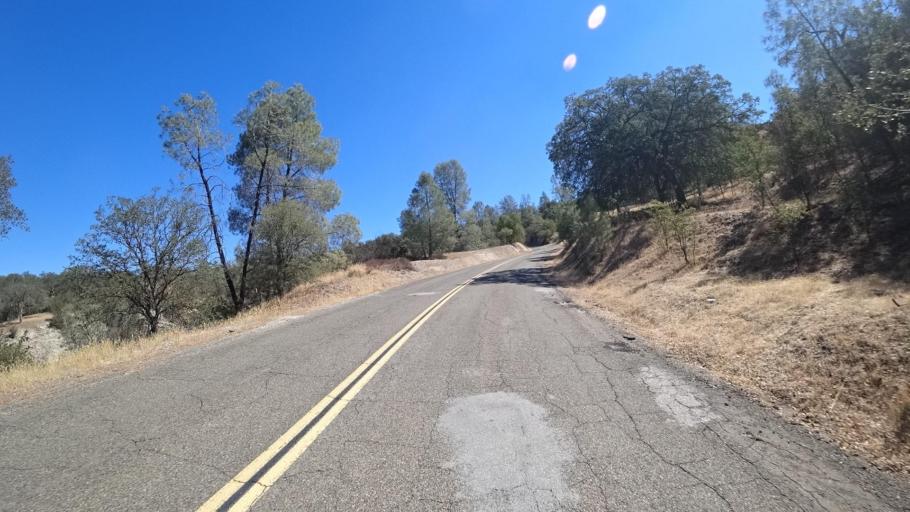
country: US
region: California
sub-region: San Luis Obispo County
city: San Miguel
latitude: 35.9096
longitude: -120.5484
